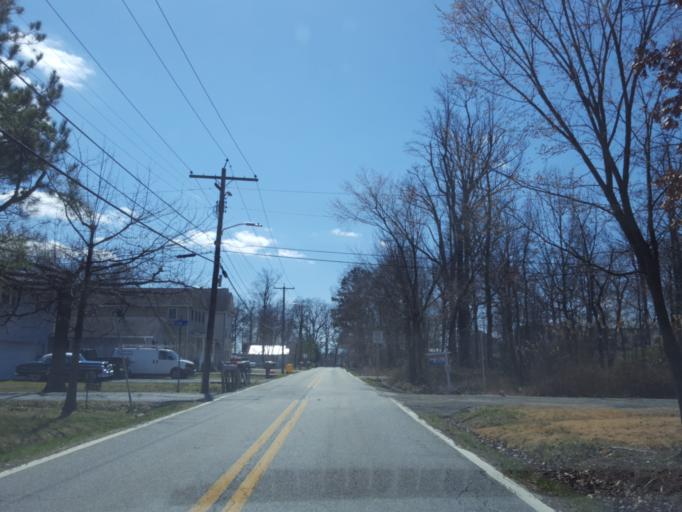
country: US
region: Maryland
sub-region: Calvert County
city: North Beach
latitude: 38.7163
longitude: -76.5287
